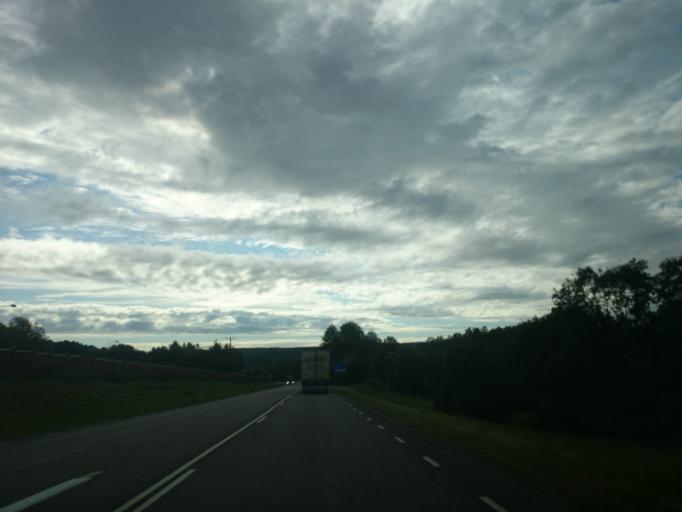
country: SE
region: Vaesternorrland
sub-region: Sundsvalls Kommun
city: Johannedal
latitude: 62.4120
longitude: 17.3743
